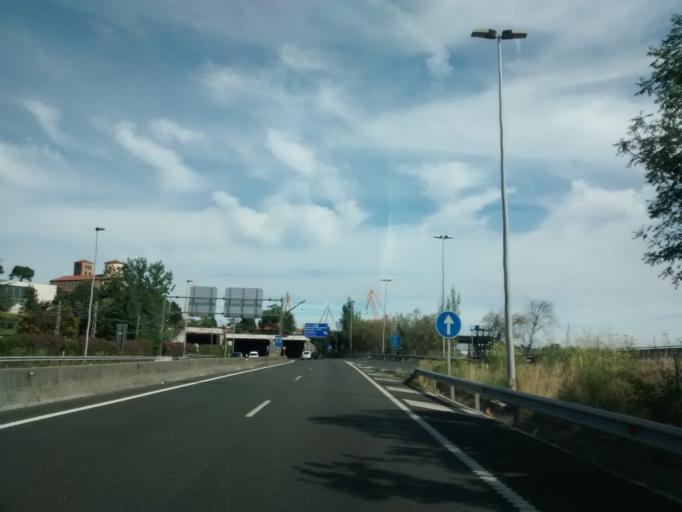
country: ES
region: Cantabria
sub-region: Provincia de Cantabria
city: El Astillero
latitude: 43.3989
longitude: -3.8152
